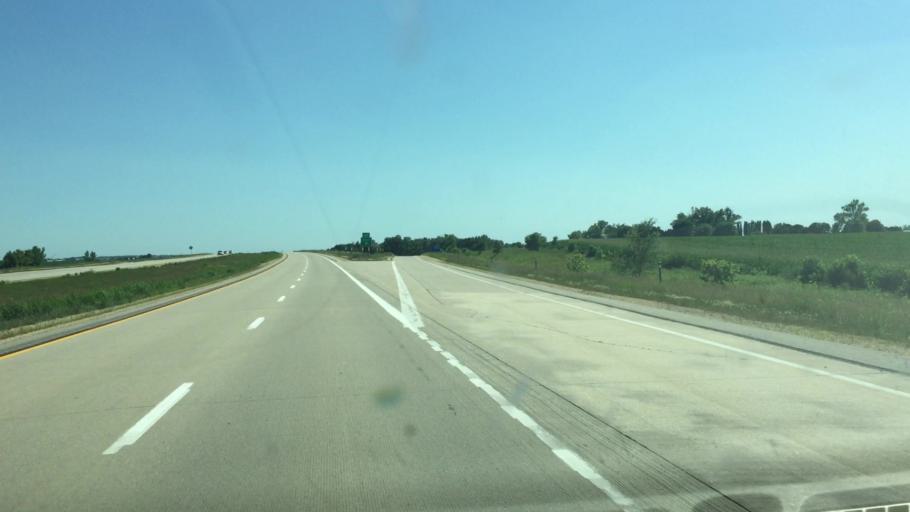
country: US
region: Iowa
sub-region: Jones County
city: Monticello
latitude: 42.2364
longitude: -91.1697
